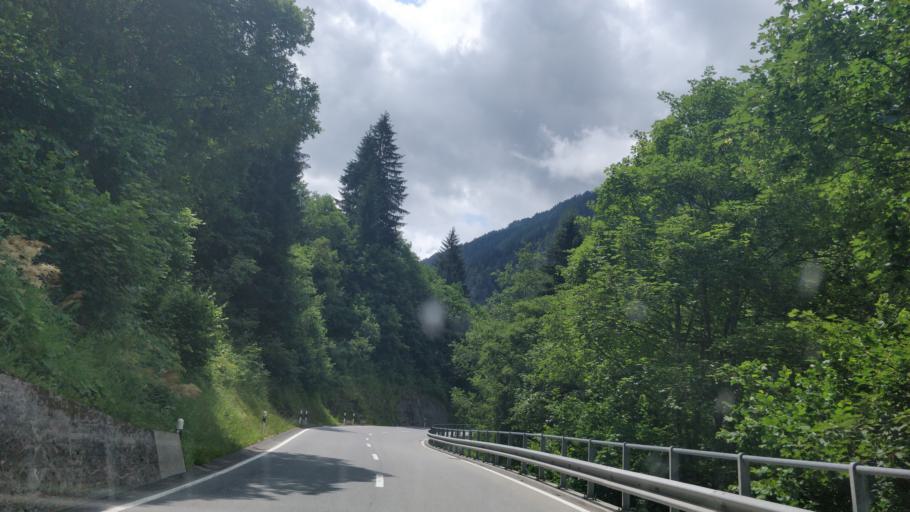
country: CH
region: Grisons
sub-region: Surselva District
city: Ilanz
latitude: 46.6546
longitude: 9.1896
